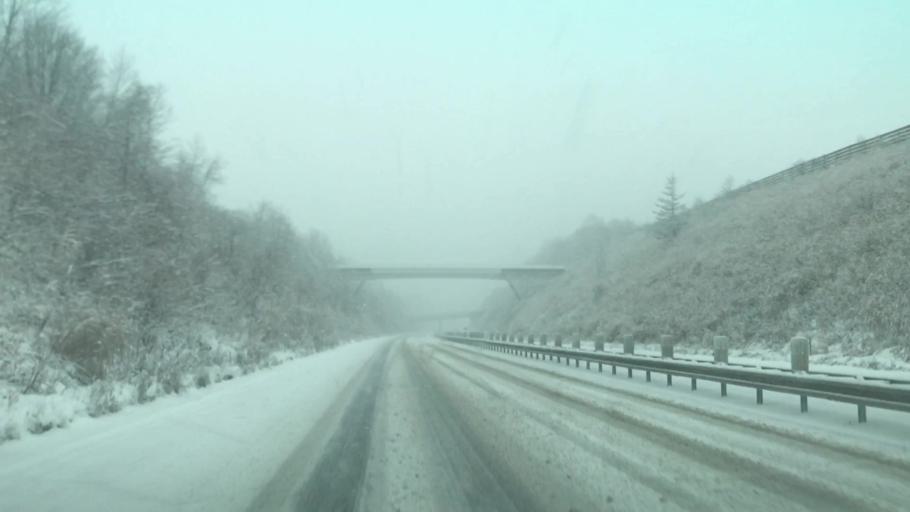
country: JP
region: Hokkaido
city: Muroran
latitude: 42.4375
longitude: 141.1336
